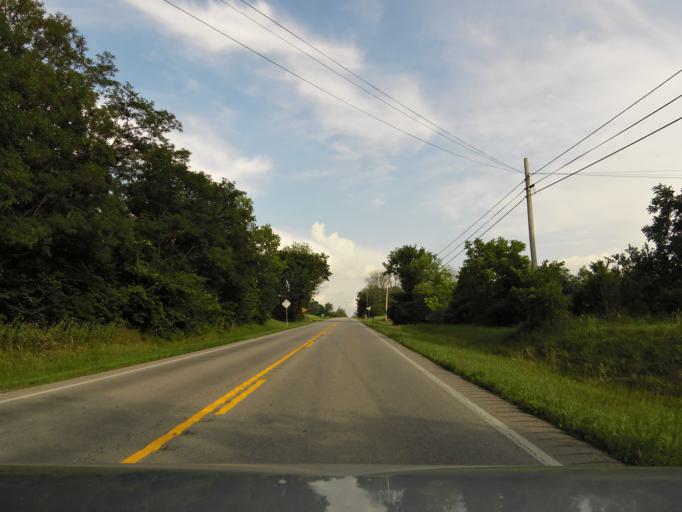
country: US
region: Kentucky
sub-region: Harrison County
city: Cynthiana
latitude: 38.3363
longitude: -84.3062
